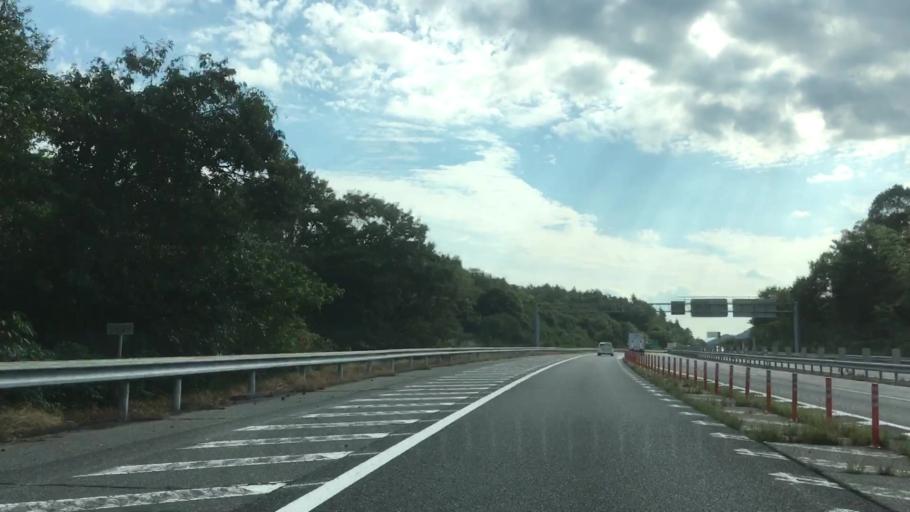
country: JP
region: Hiroshima
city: Miyajima
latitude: 34.3291
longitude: 132.2936
